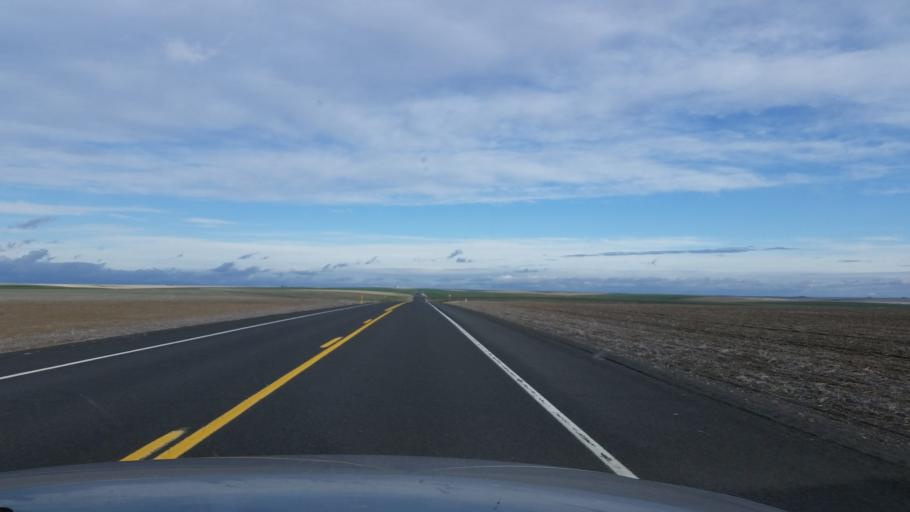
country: US
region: Washington
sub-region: Adams County
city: Ritzville
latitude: 47.3907
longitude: -118.4114
